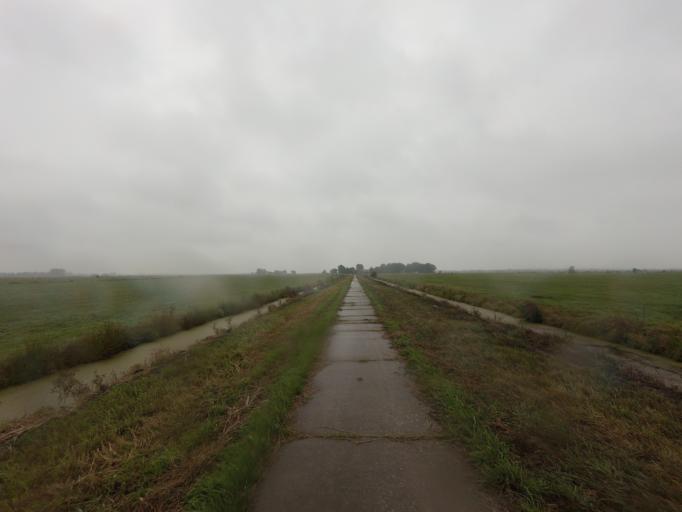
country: NL
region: Friesland
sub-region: Gemeente Boarnsterhim
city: Nes
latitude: 53.0338
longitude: 5.8746
